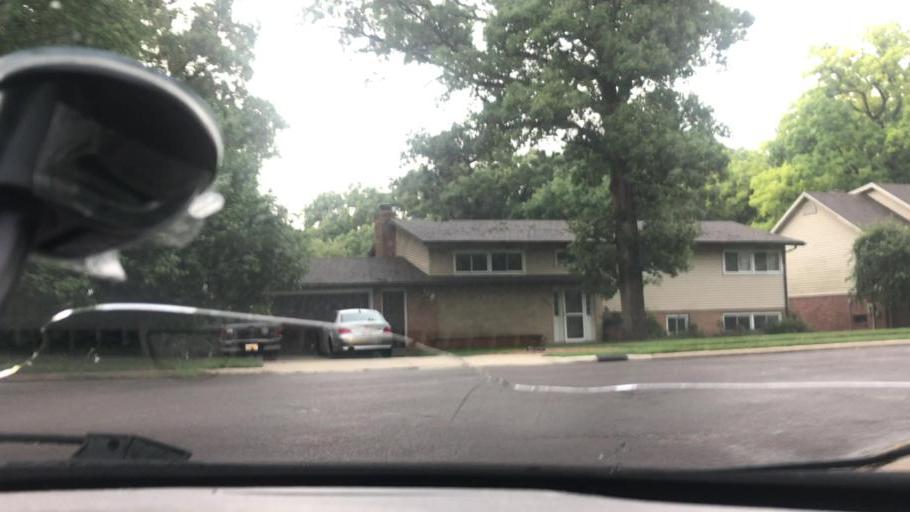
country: US
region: Illinois
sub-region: Tazewell County
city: Pekin
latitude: 40.5441
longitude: -89.6189
